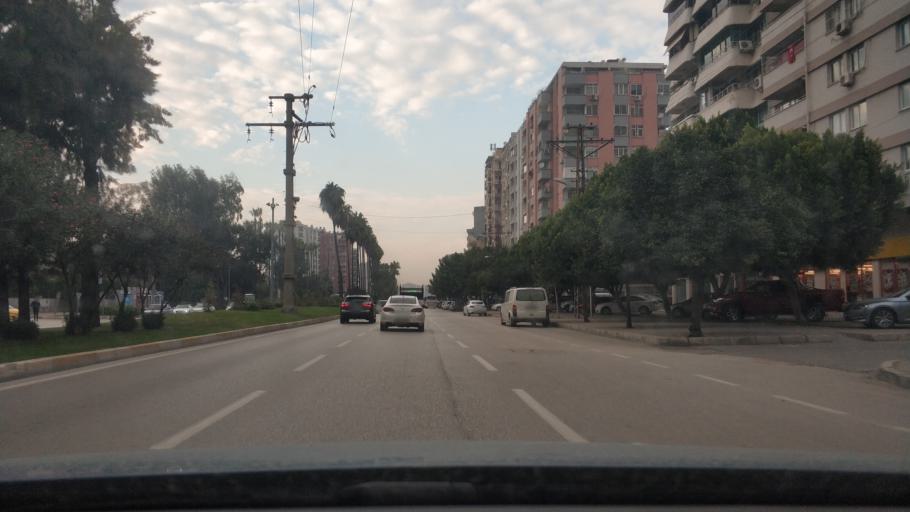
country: TR
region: Adana
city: Adana
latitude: 36.9997
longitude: 35.3162
